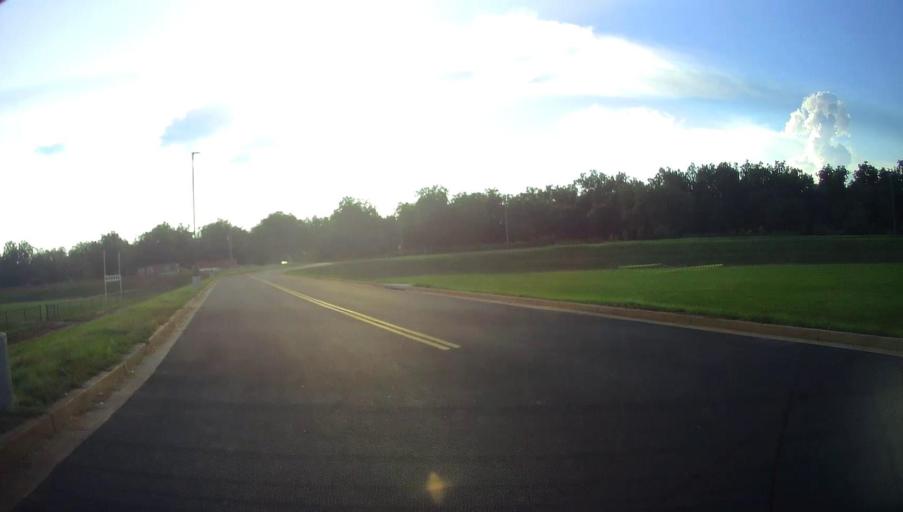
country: US
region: Georgia
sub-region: Peach County
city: Fort Valley
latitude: 32.5929
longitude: -83.8413
